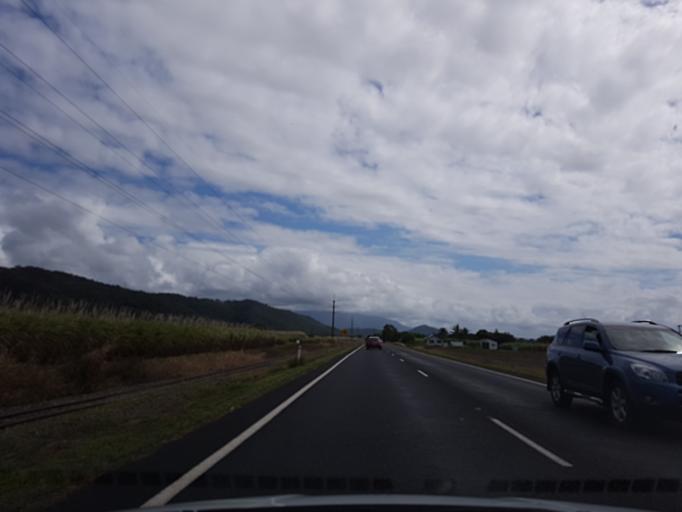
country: AU
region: Queensland
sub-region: Cairns
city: Port Douglas
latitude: -16.5056
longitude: 145.4382
